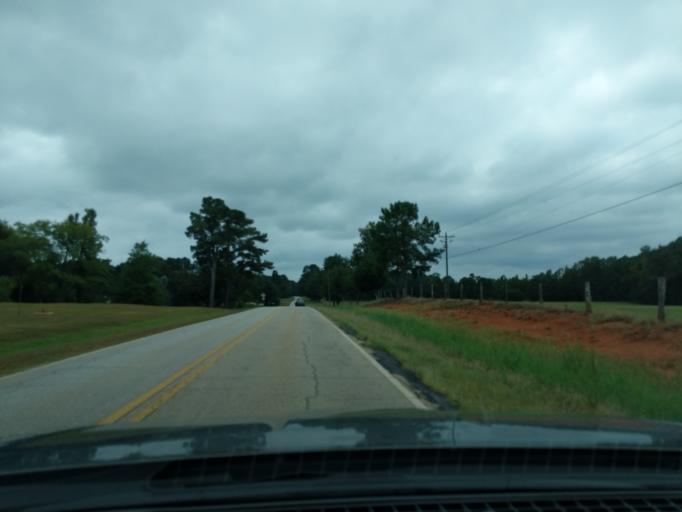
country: US
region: Georgia
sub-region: Columbia County
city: Appling
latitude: 33.6322
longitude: -82.3993
